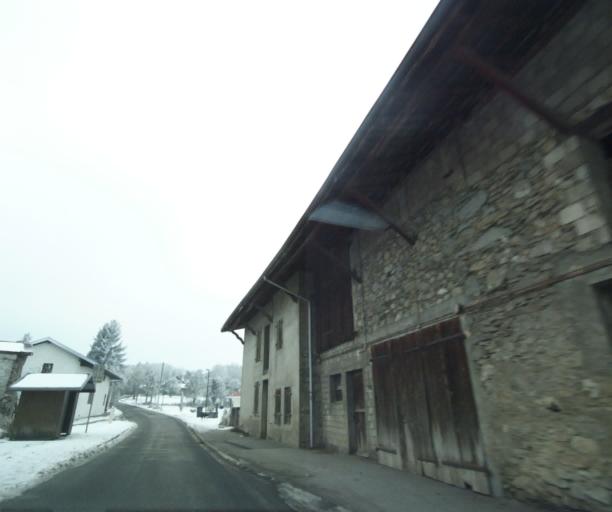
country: FR
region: Rhone-Alpes
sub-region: Departement de la Haute-Savoie
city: Reignier-Esery
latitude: 46.1254
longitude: 6.2423
